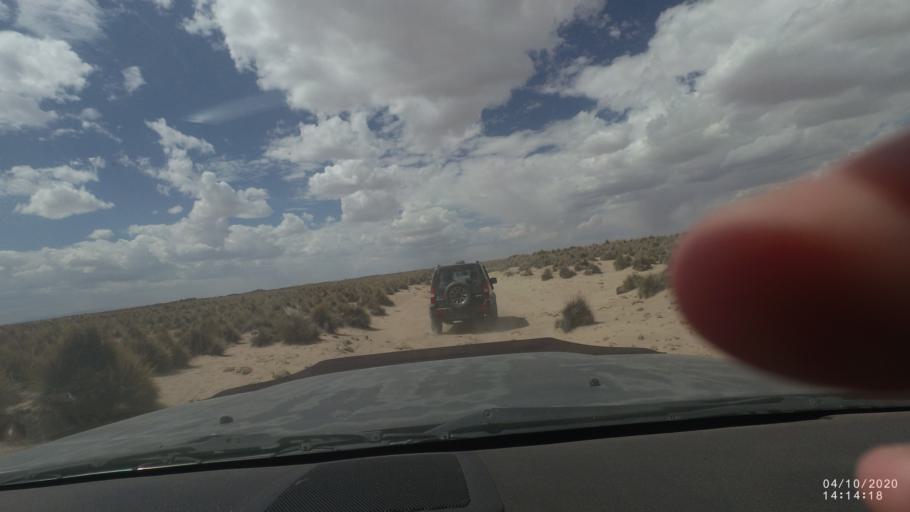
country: BO
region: Oruro
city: Poopo
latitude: -18.6955
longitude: -67.4549
